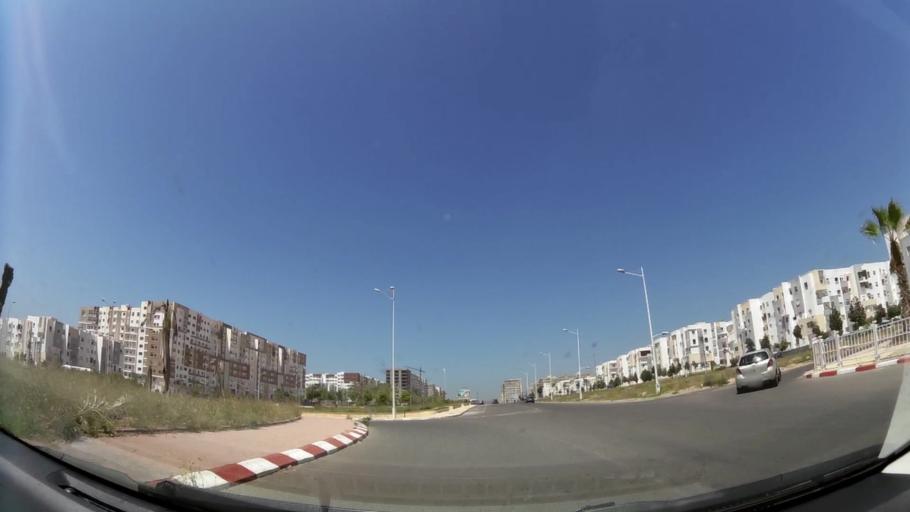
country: MA
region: Oued ed Dahab-Lagouira
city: Dakhla
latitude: 30.4344
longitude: -9.5570
